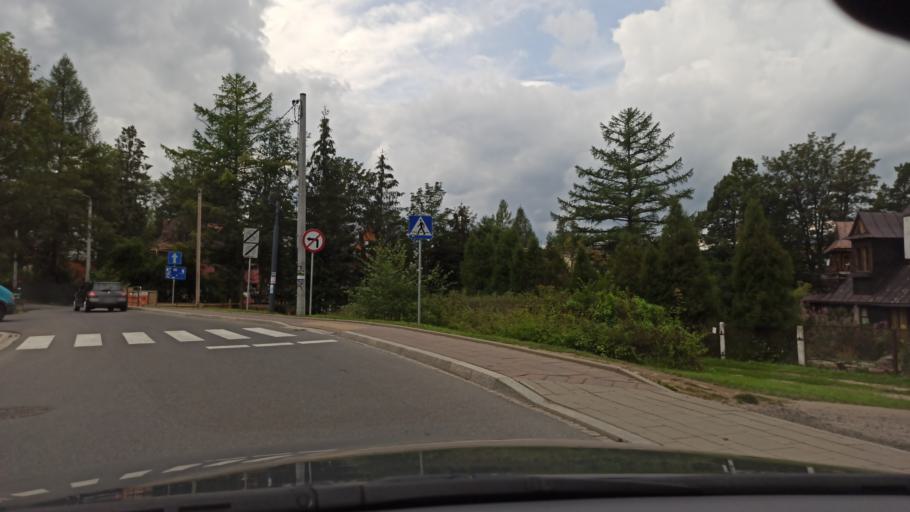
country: PL
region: Lesser Poland Voivodeship
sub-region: Powiat tatrzanski
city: Zakopane
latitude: 49.2903
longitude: 19.9701
